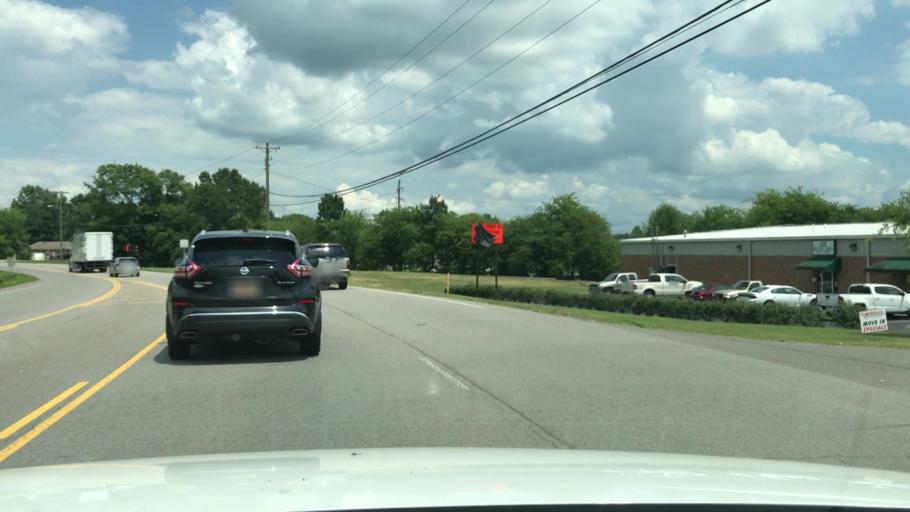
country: US
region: Tennessee
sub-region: Sumner County
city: Gallatin
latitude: 36.3638
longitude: -86.4379
